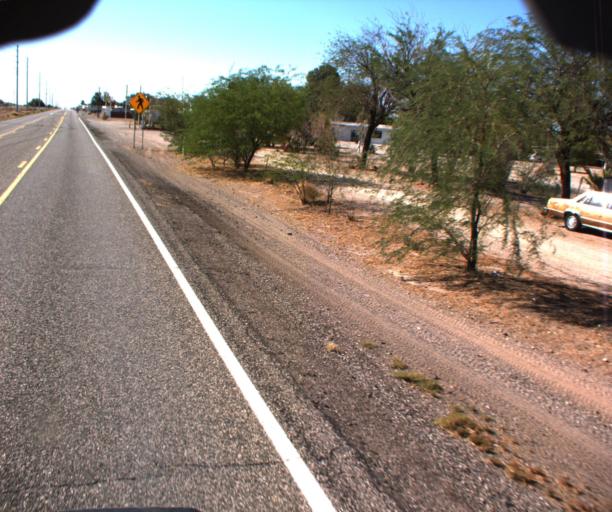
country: US
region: Arizona
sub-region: La Paz County
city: Cienega Springs
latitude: 33.9363
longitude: -114.0088
